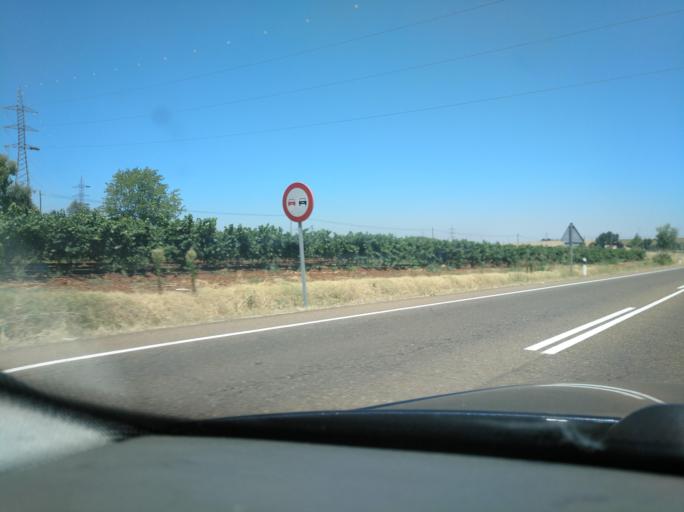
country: ES
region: Extremadura
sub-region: Provincia de Badajoz
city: Olivenza
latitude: 38.7376
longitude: -7.0665
